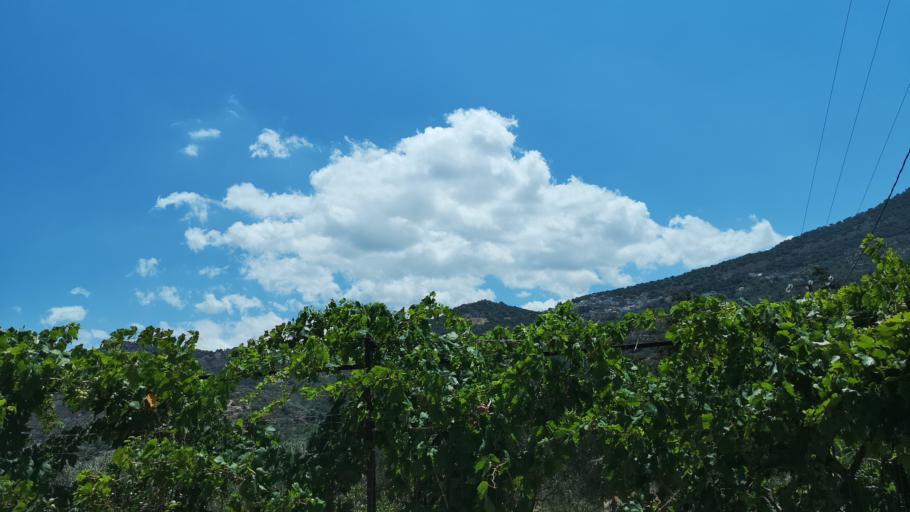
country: GR
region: Crete
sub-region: Nomos Lasithiou
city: Neapoli
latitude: 35.2500
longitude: 25.6233
